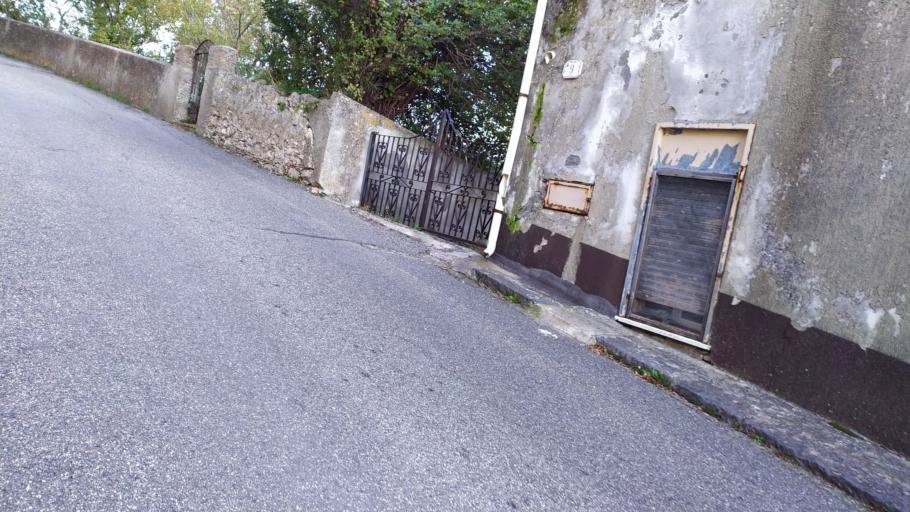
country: IT
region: Sicily
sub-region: Messina
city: Rometta
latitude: 38.1699
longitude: 15.4154
